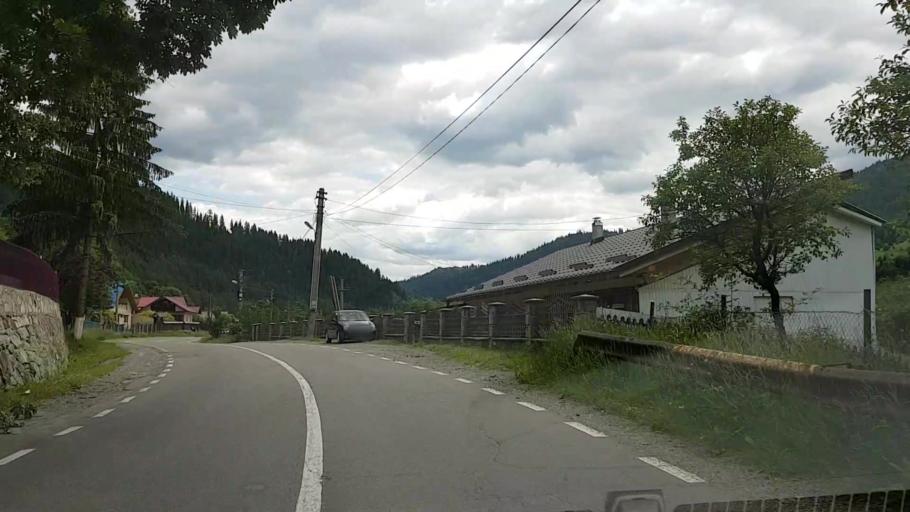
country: RO
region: Neamt
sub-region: Comuna Poiana Teiului
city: Poiana Teiului
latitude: 47.1312
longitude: 25.8993
